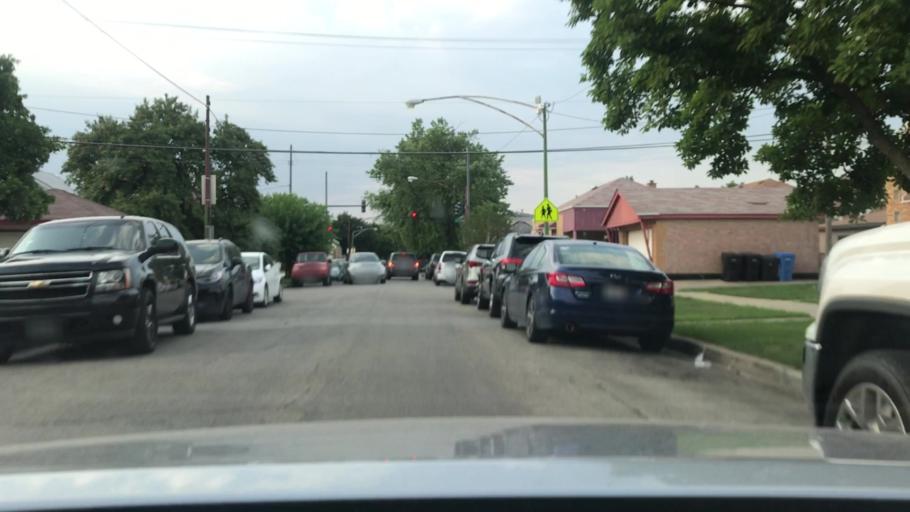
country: US
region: Illinois
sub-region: Cook County
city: Hometown
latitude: 41.7634
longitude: -87.7175
